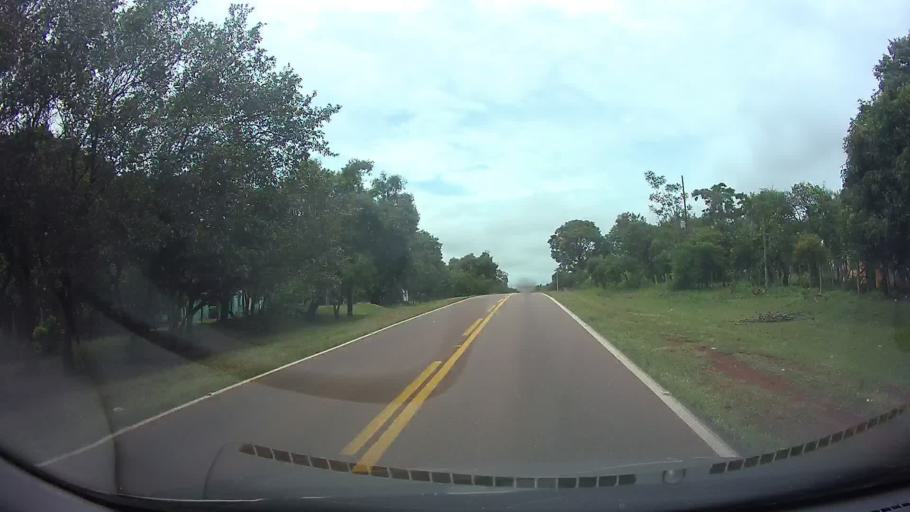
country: PY
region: Paraguari
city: Acahay
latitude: -25.8494
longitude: -57.1431
